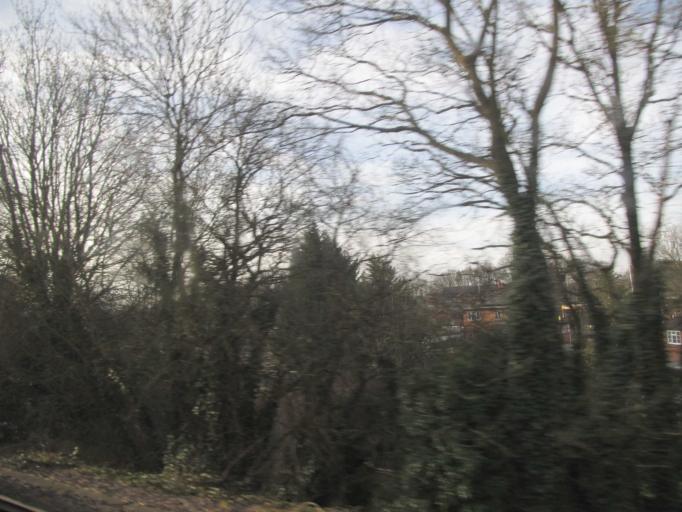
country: GB
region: England
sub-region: Wokingham
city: Wokingham
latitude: 51.4204
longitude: -0.8545
